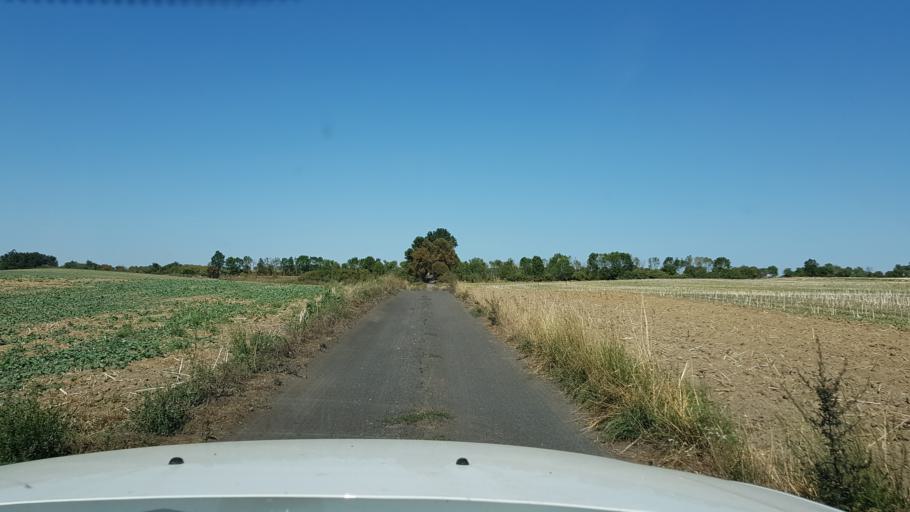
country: PL
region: West Pomeranian Voivodeship
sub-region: Powiat gryfinski
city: Moryn
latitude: 52.8608
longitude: 14.3552
